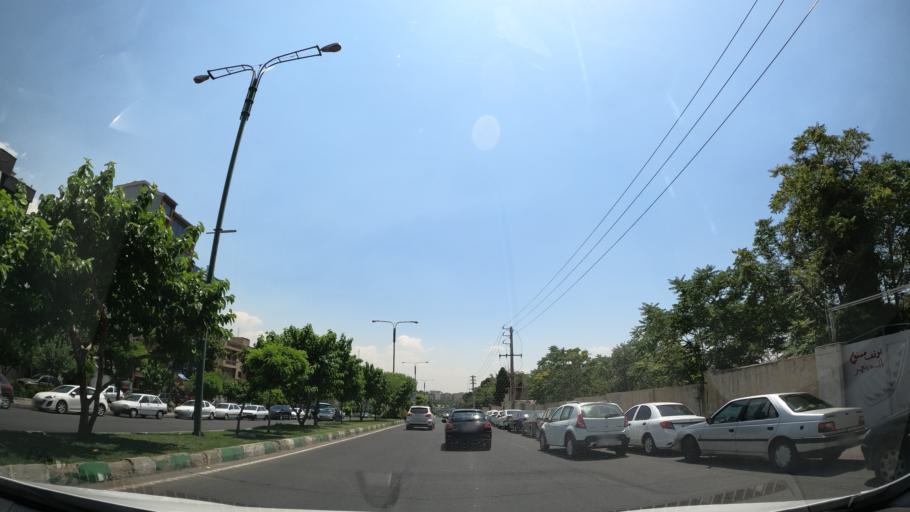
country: IR
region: Tehran
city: Tajrish
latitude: 35.7708
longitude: 51.3799
